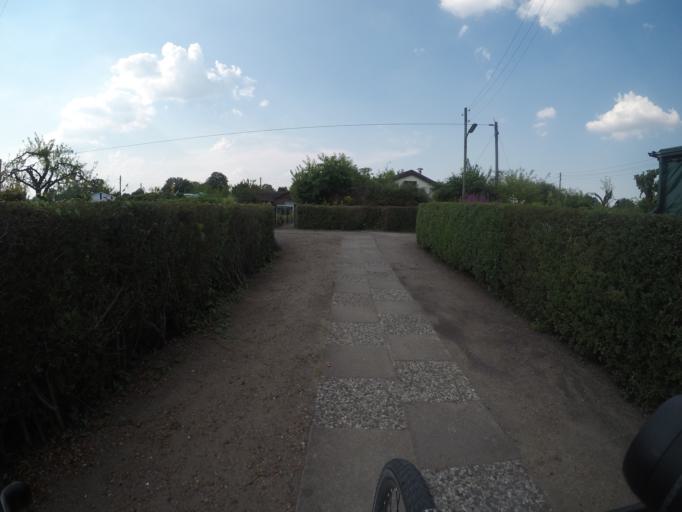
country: DE
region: Hamburg
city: Wandsbek
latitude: 53.5615
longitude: 10.0921
